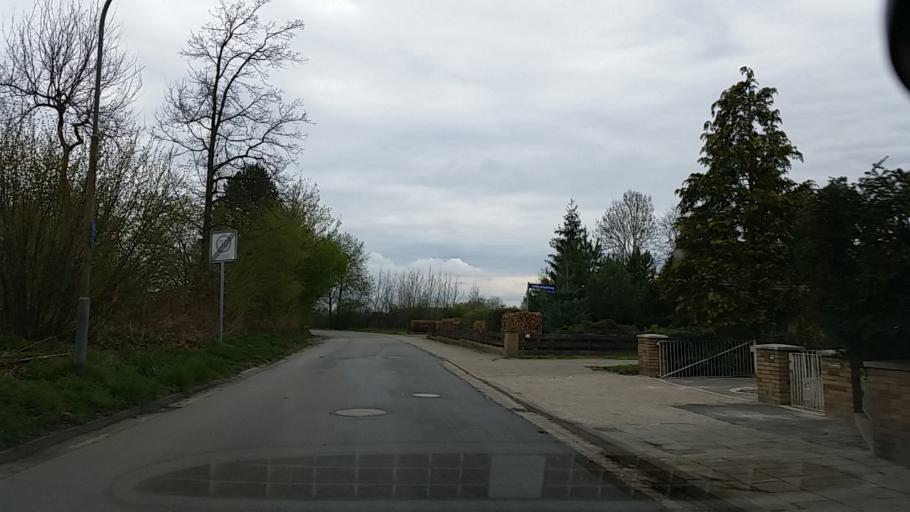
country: DE
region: Lower Saxony
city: Meine
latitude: 52.3920
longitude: 10.5393
